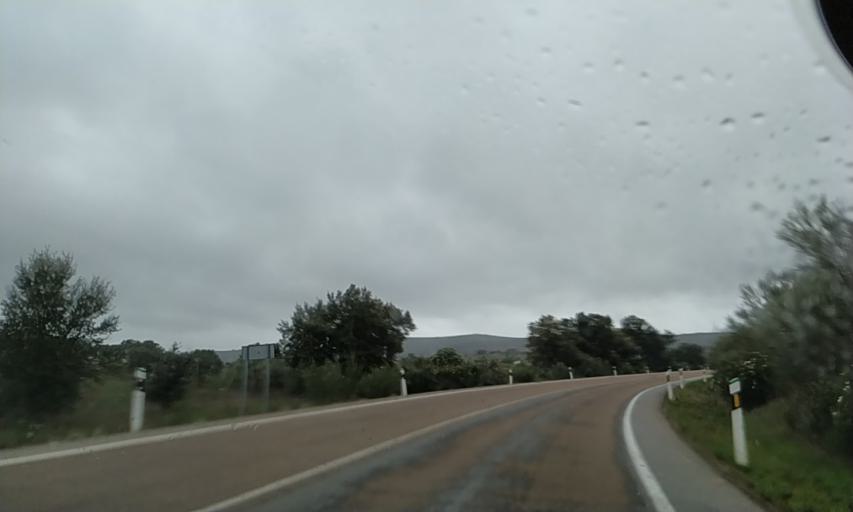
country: ES
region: Extremadura
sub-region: Provincia de Badajoz
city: Puebla de Obando
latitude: 39.2728
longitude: -6.5204
